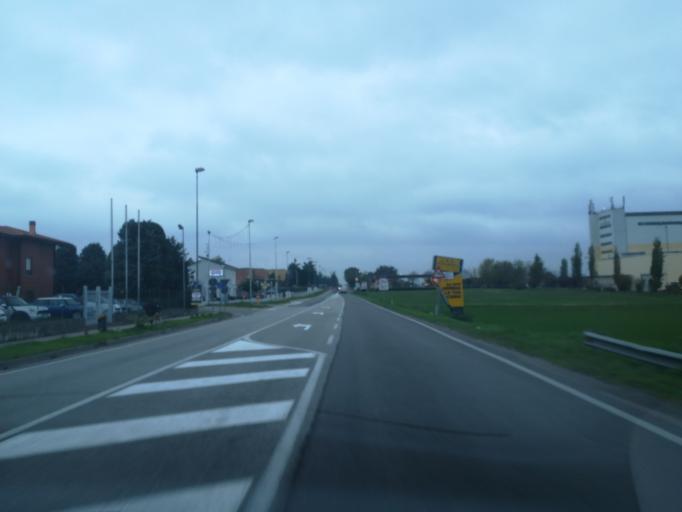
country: IT
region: Emilia-Romagna
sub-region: Provincia di Bologna
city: Toscanella
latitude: 44.3849
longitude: 11.6332
